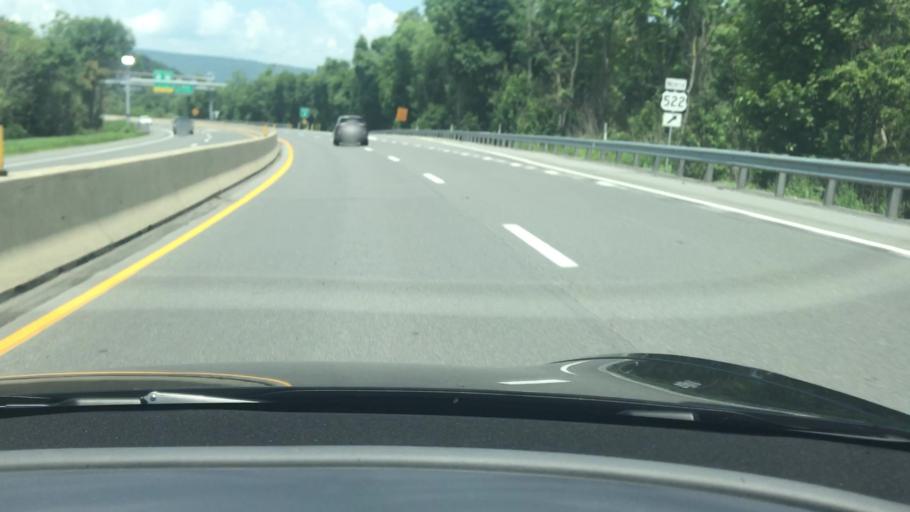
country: US
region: Pennsylvania
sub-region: Mifflin County
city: Lewistown
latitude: 40.6036
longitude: -77.5627
